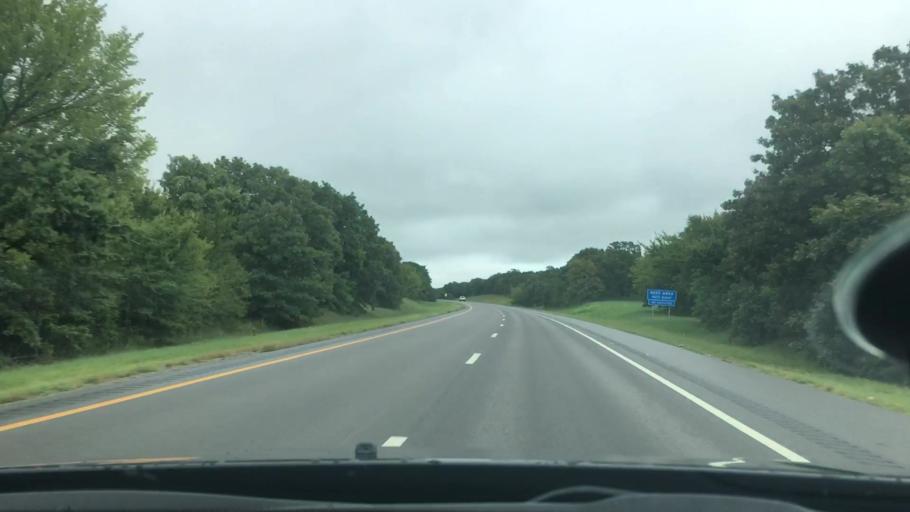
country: US
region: Oklahoma
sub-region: Okmulgee County
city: Morris
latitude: 35.4341
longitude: -95.7962
